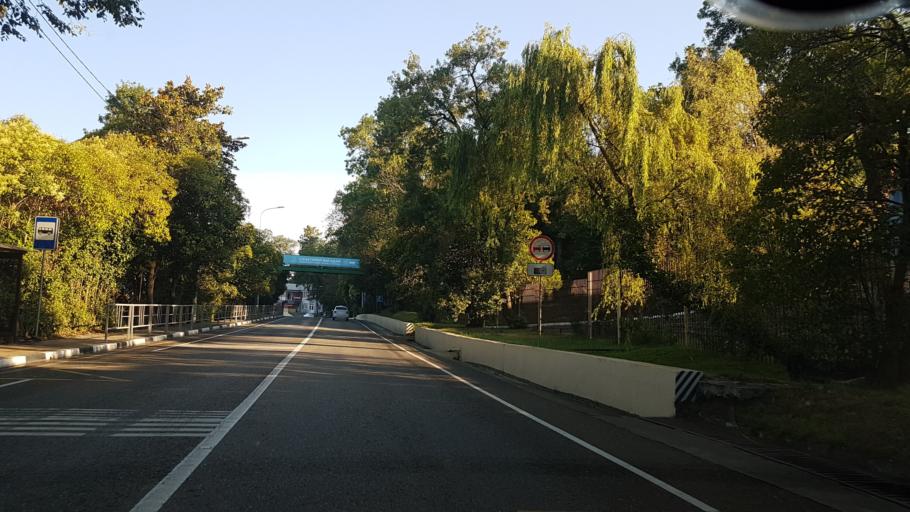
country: RU
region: Krasnodarskiy
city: Gornoye Loo
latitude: 43.6867
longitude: 39.5968
